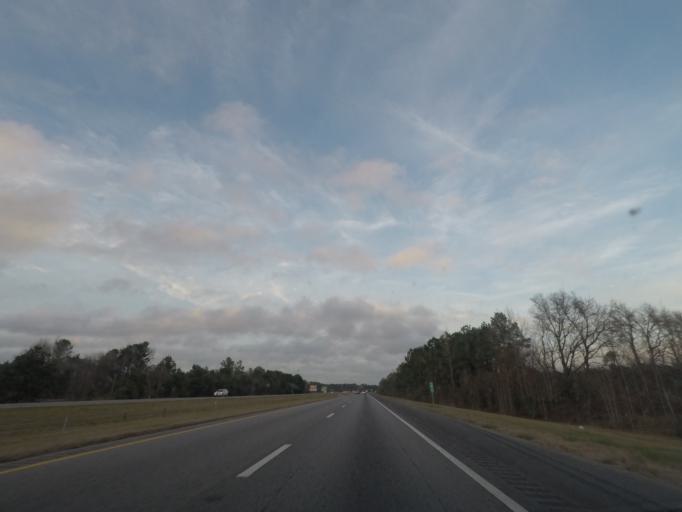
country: US
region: South Carolina
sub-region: Orangeburg County
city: Holly Hill
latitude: 33.3902
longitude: -80.5157
